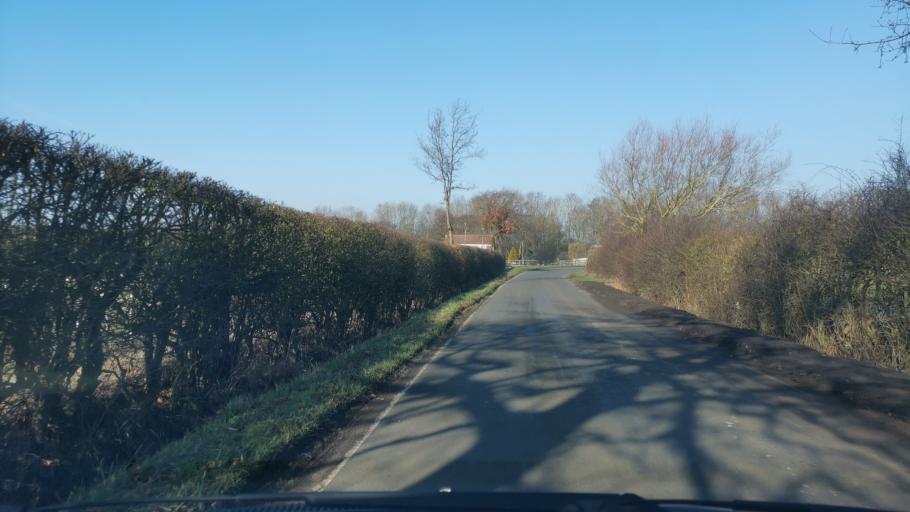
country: GB
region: England
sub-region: City of York
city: Murton
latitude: 53.9758
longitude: -1.0165
